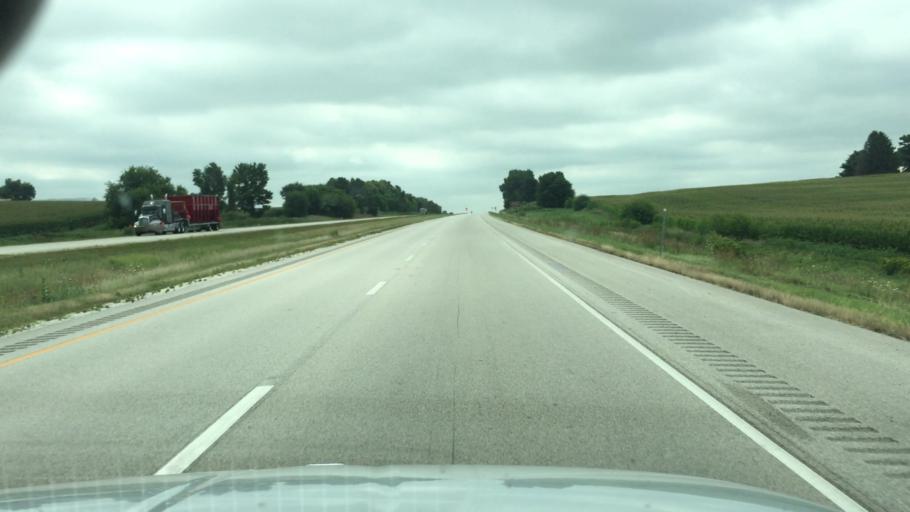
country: US
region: Illinois
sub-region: Henry County
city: Orion
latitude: 41.3126
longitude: -90.3342
